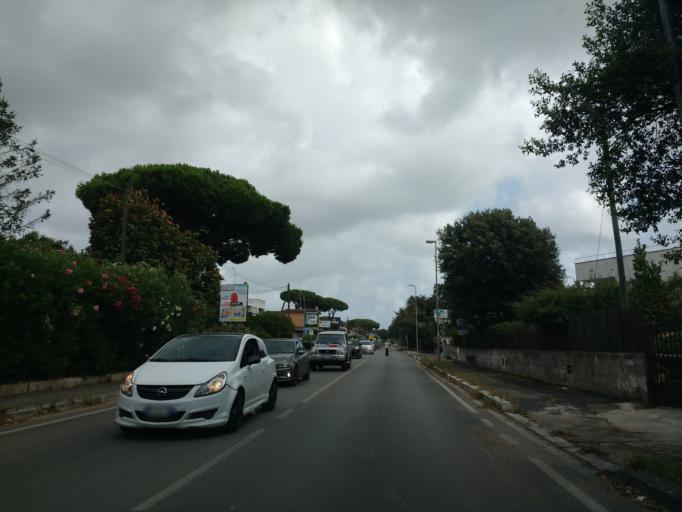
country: IT
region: Latium
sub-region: Citta metropolitana di Roma Capitale
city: Anzio
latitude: 41.4856
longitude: 12.6005
